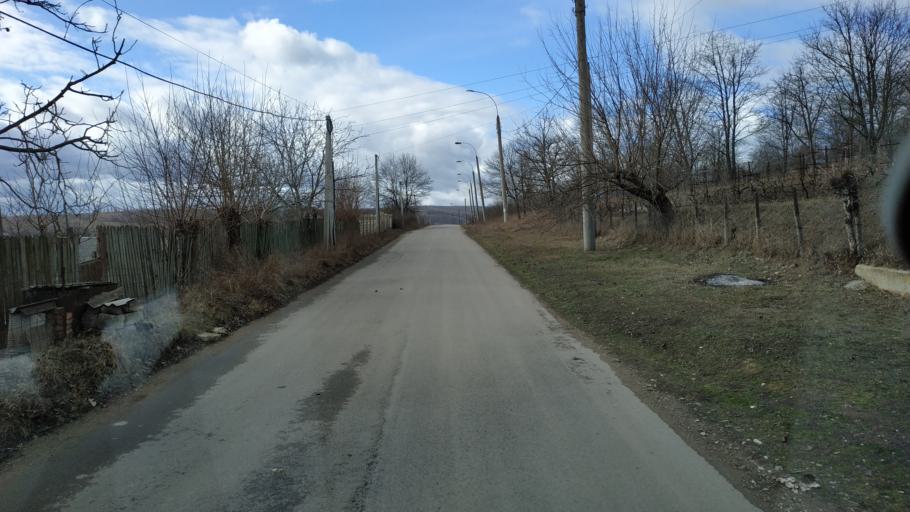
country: MD
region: Stinga Nistrului
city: Bucovat
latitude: 47.1876
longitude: 28.4689
